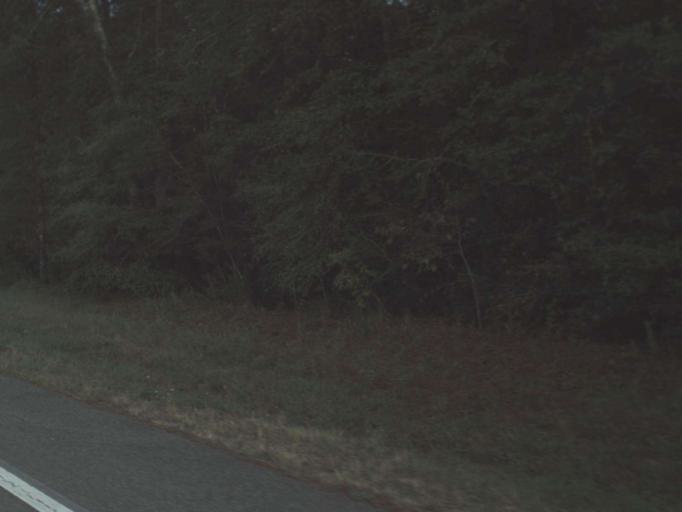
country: US
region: Florida
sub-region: Walton County
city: DeFuniak Springs
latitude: 30.9059
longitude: -86.1318
